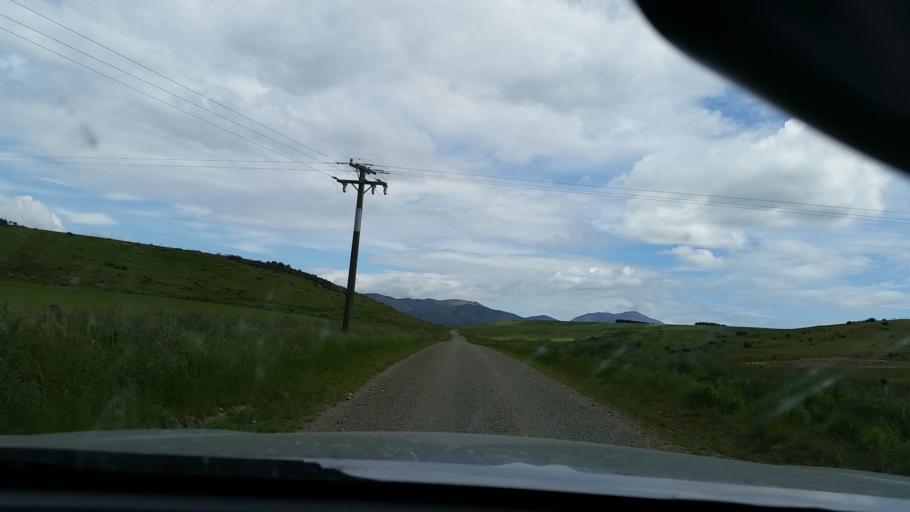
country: NZ
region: Southland
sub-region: Southland District
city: Winton
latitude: -45.7315
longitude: 168.1309
